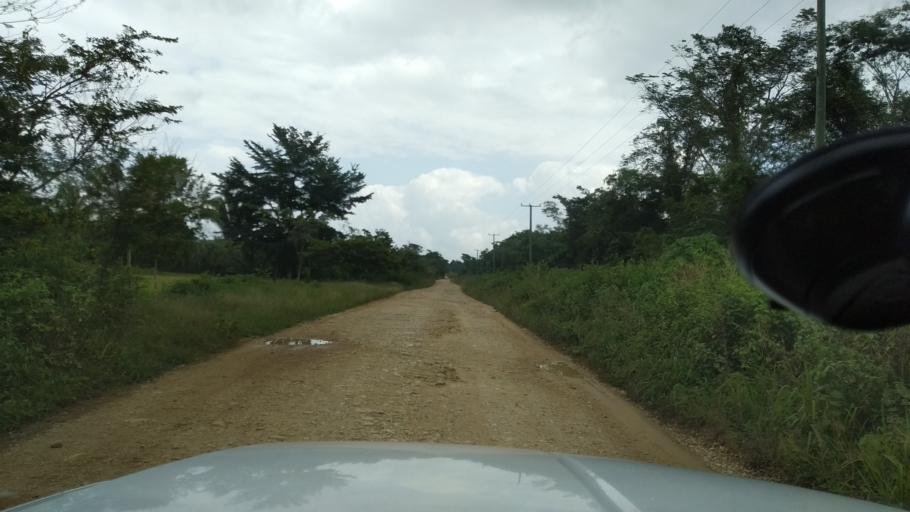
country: BZ
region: Toledo
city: Punta Gorda
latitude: 16.2180
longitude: -89.0018
